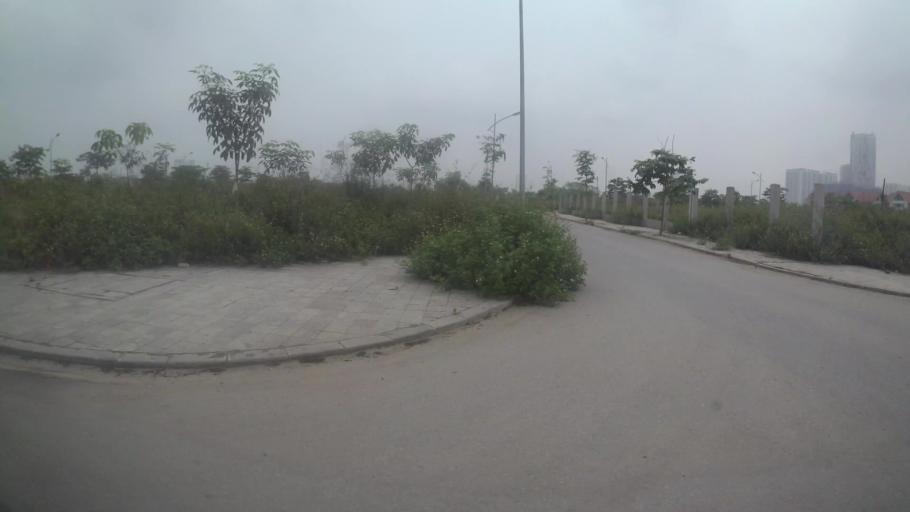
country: VN
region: Ha Noi
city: Ha Dong
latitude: 20.9775
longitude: 105.7528
